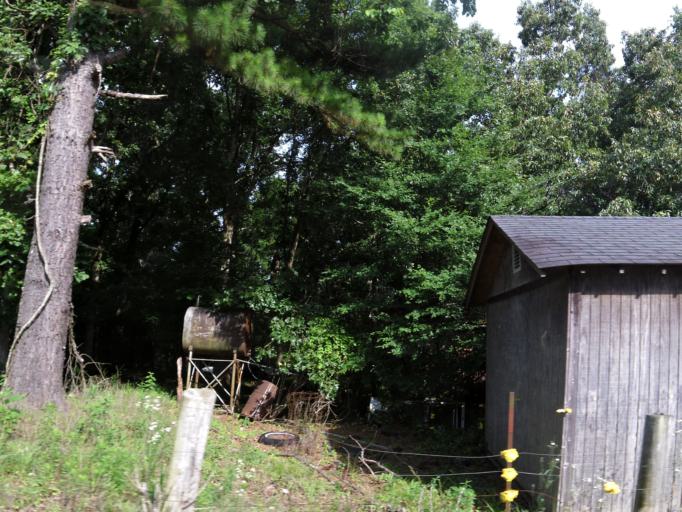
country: US
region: Tennessee
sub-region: Benton County
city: Camden
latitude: 36.0511
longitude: -88.1669
